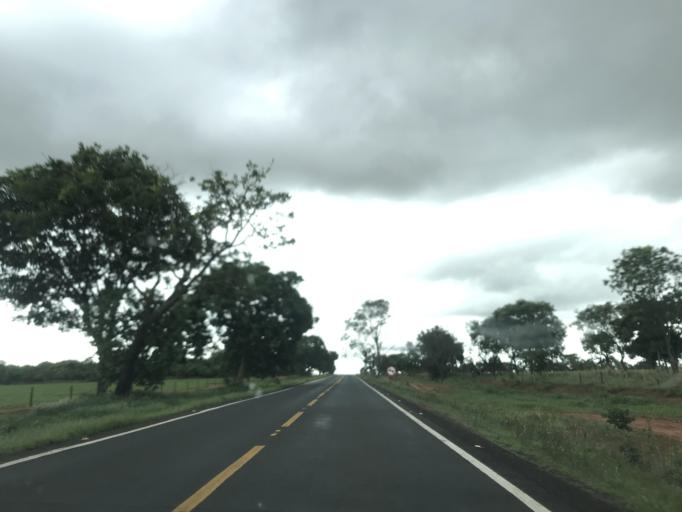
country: BR
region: Goias
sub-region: Caldas Novas
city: Caldas Novas
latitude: -17.6293
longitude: -48.7060
